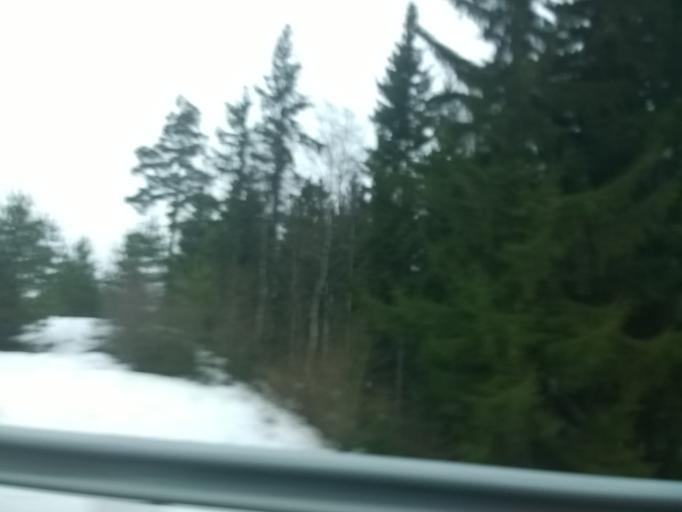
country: FI
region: Pirkanmaa
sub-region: Tampere
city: Lempaeaelae
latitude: 61.3261
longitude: 23.7754
